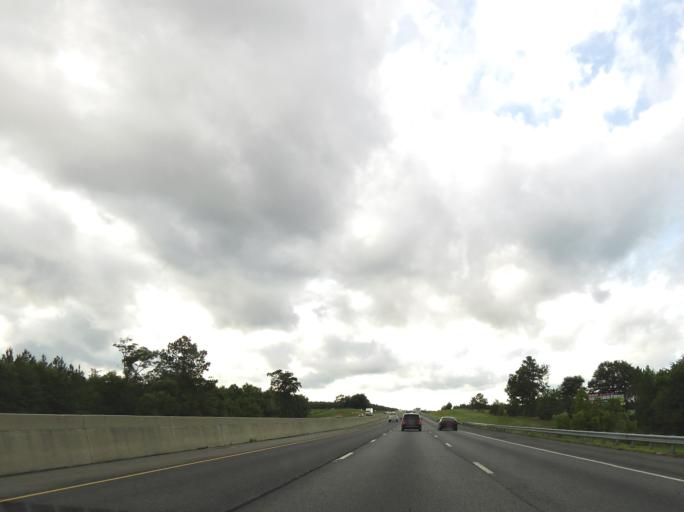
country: US
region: Georgia
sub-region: Turner County
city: Ashburn
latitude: 31.7999
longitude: -83.7006
